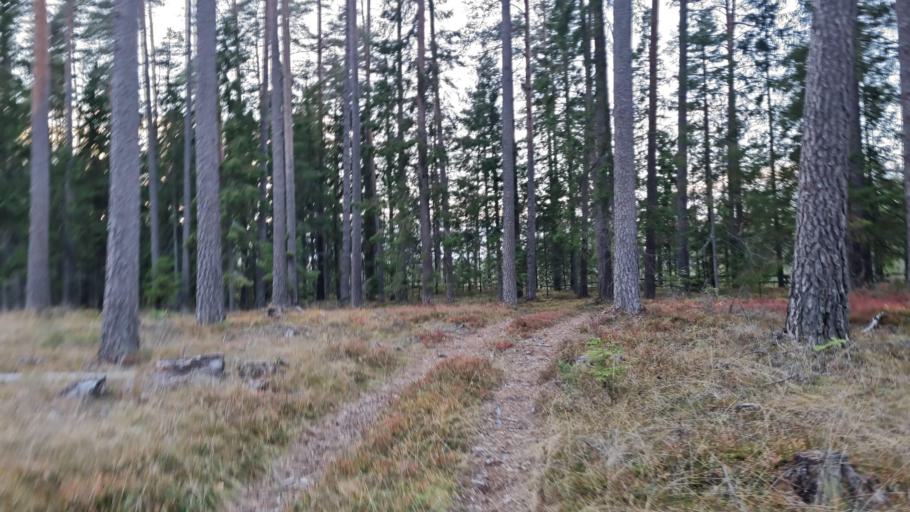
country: LV
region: Mazsalaca
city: Mazsalaca
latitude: 57.8926
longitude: 25.0129
